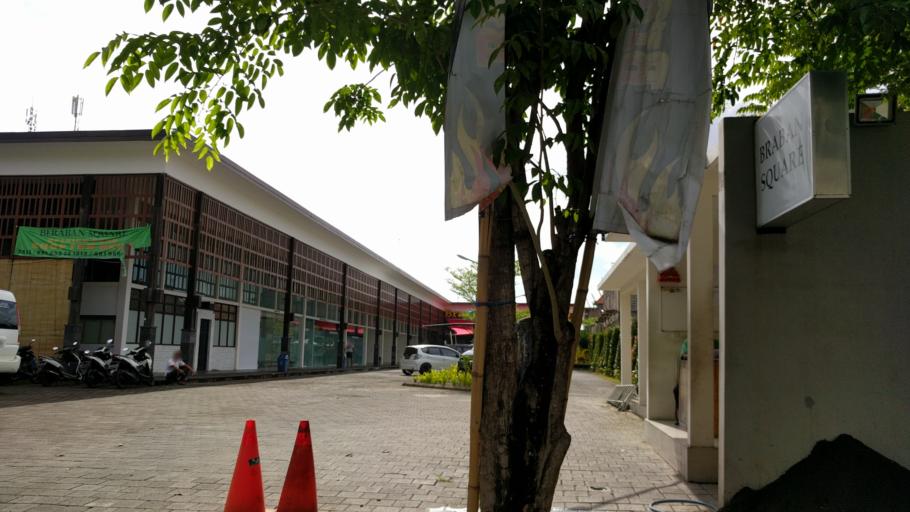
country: ID
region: Bali
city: Kuta
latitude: -8.6801
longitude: 115.1629
